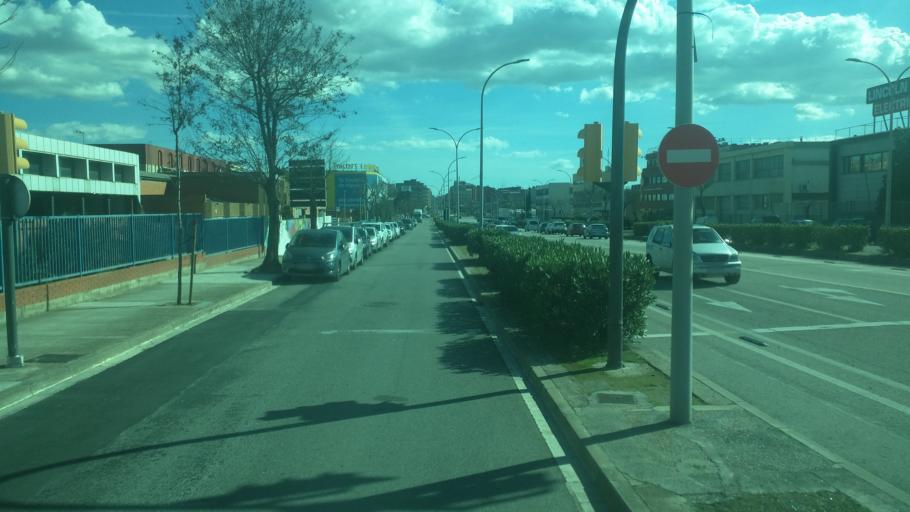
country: ES
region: Catalonia
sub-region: Provincia de Barcelona
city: Sant Feliu de Llobregat
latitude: 41.3907
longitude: 2.0377
